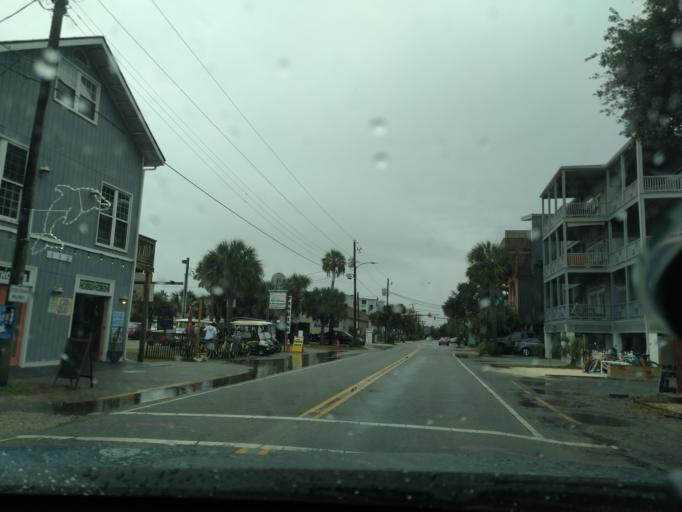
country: US
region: South Carolina
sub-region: Charleston County
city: Folly Beach
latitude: 32.6560
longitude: -79.9396
